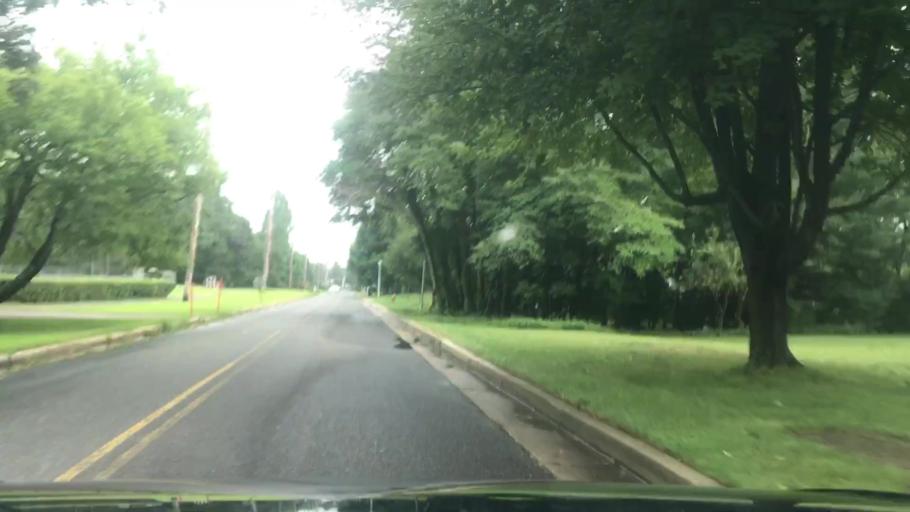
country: US
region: New Jersey
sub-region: Monmouth County
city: Little Silver
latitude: 40.3478
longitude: -74.0403
